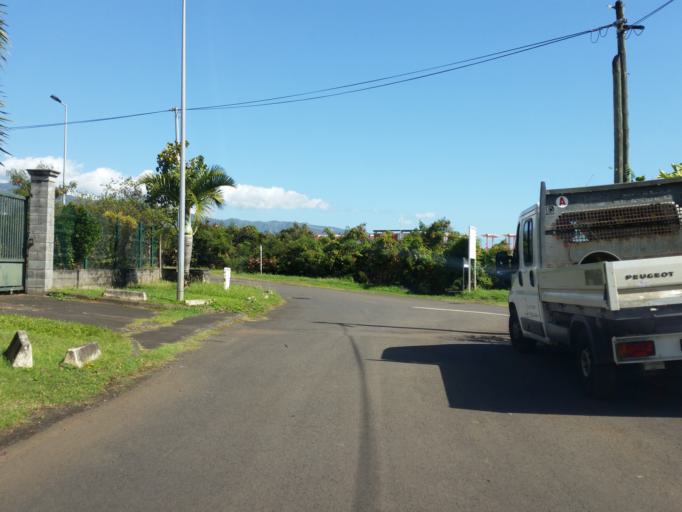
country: RE
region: Reunion
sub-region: Reunion
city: Sainte-Marie
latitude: -20.8963
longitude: 55.5304
